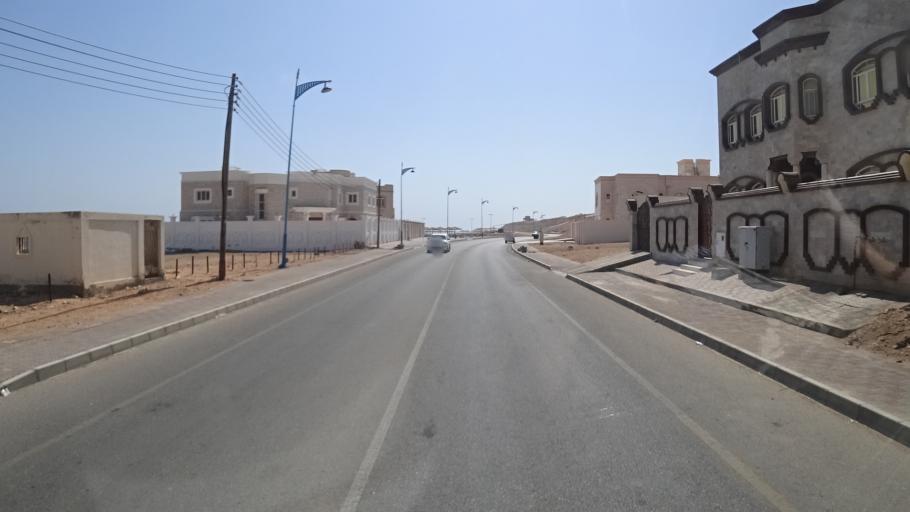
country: OM
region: Ash Sharqiyah
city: Sur
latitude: 22.5670
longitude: 59.5556
